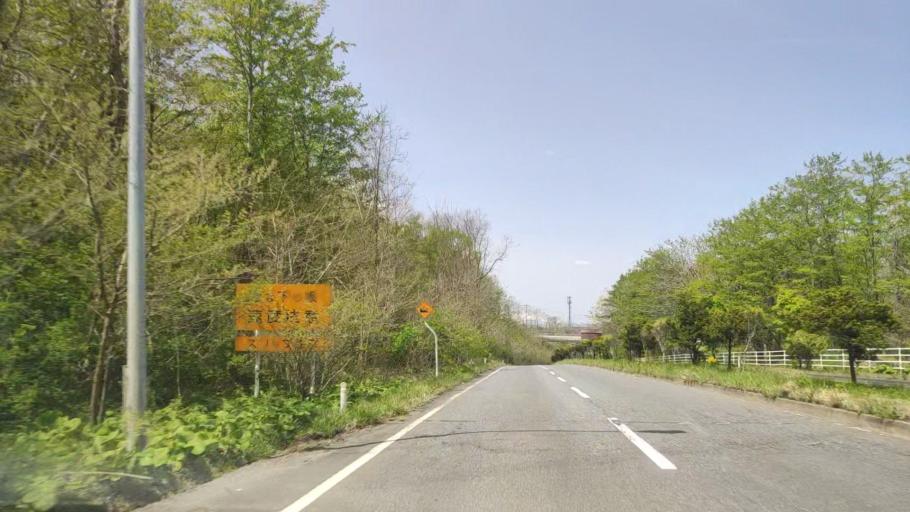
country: JP
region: Aomori
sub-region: Hachinohe Shi
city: Uchimaru
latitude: 40.4955
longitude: 141.4616
